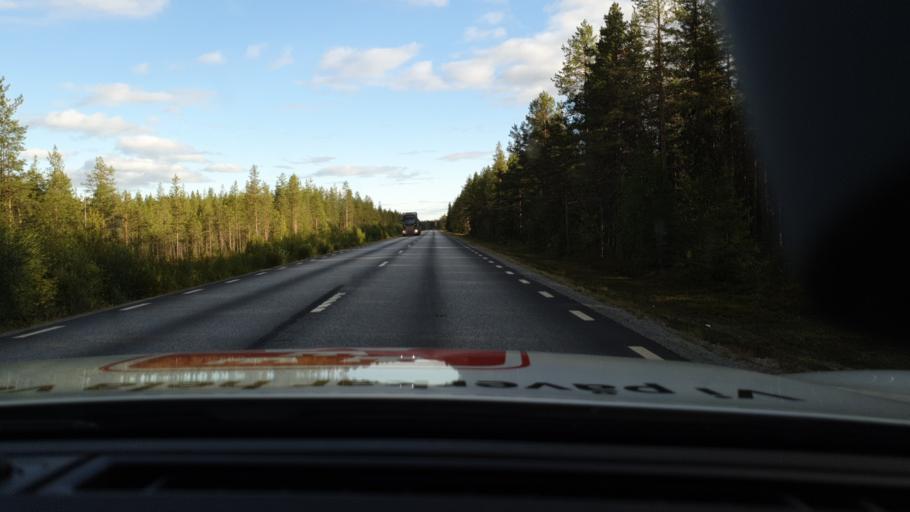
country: SE
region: Norrbotten
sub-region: Overkalix Kommun
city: OEverkalix
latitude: 66.6177
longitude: 22.2337
